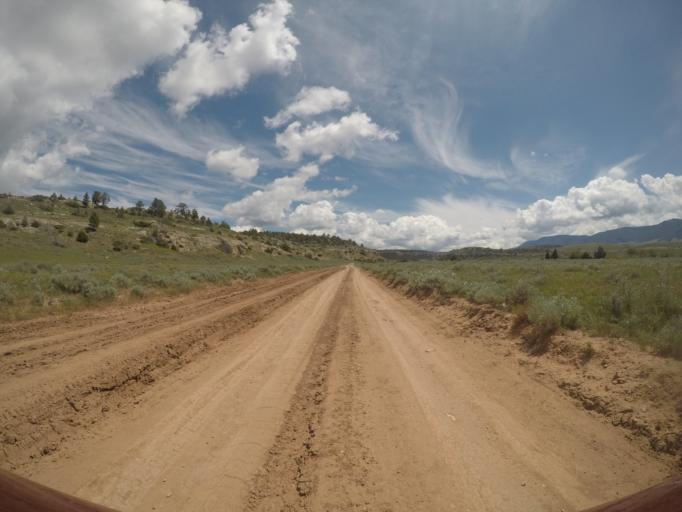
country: US
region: Montana
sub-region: Yellowstone County
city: Laurel
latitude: 45.2438
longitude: -108.6548
